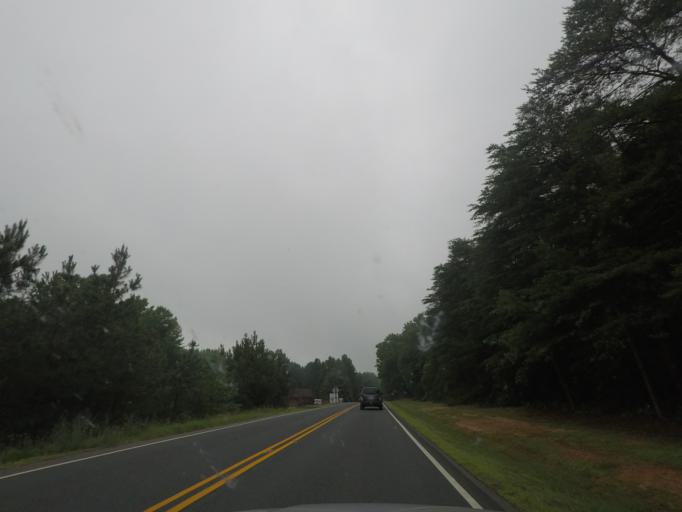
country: US
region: Virginia
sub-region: Charlotte County
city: Charlotte Court House
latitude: 37.0748
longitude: -78.4770
